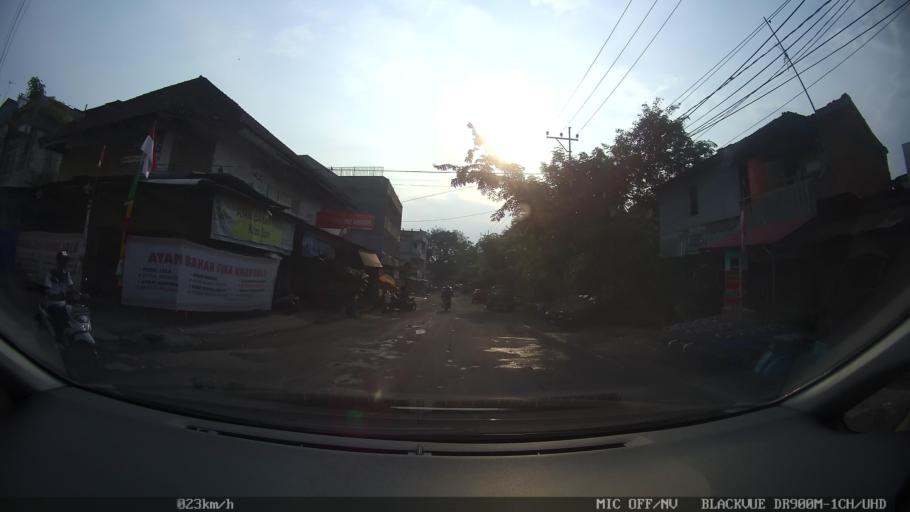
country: ID
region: Lampung
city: Bandarlampung
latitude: -5.4488
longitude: 105.2688
